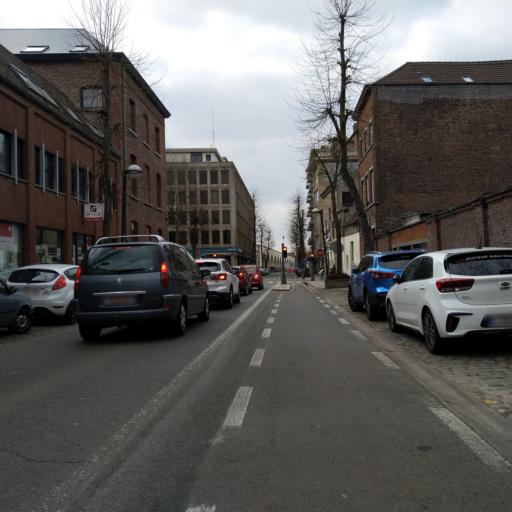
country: BE
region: Wallonia
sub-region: Province du Hainaut
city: Mons
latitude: 50.4474
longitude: 3.9490
